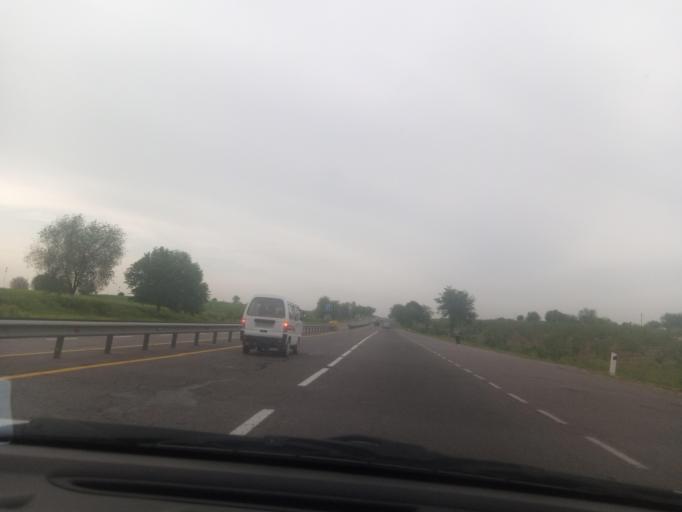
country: UZ
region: Toshkent
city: Tuytepa
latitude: 41.1144
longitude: 69.4461
